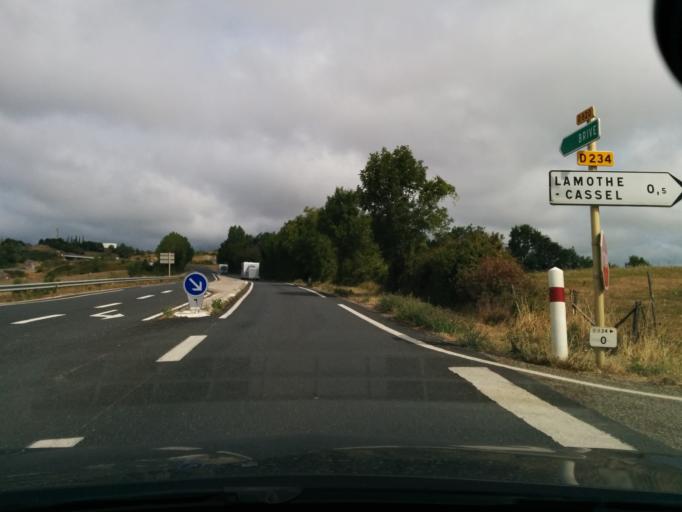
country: FR
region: Midi-Pyrenees
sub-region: Departement du Lot
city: Le Vigan
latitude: 44.6079
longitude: 1.5045
